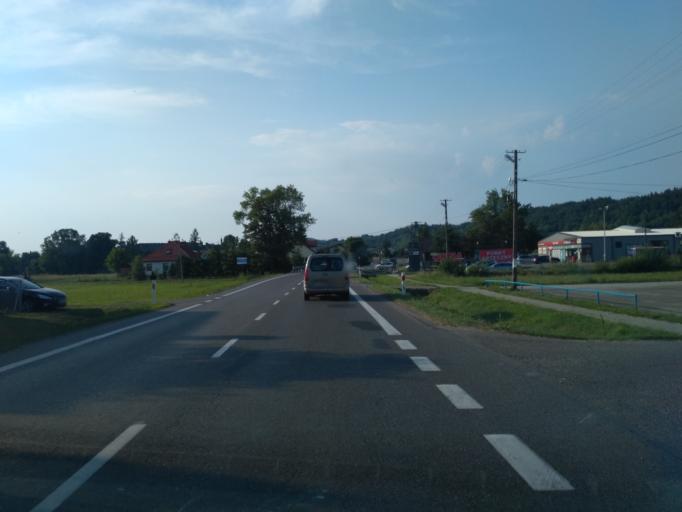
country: PL
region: Subcarpathian Voivodeship
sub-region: Powiat brzozowski
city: Stara Wies
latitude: 49.7166
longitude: 22.0116
